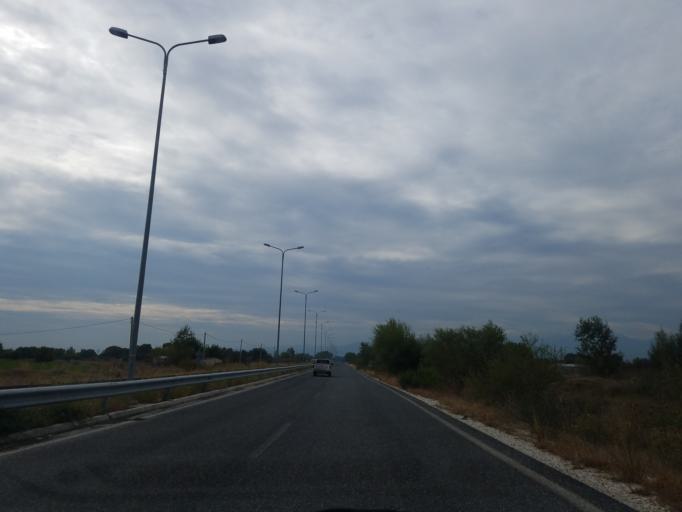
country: GR
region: Thessaly
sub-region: Trikala
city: Pyrgetos
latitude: 39.5561
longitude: 21.7337
